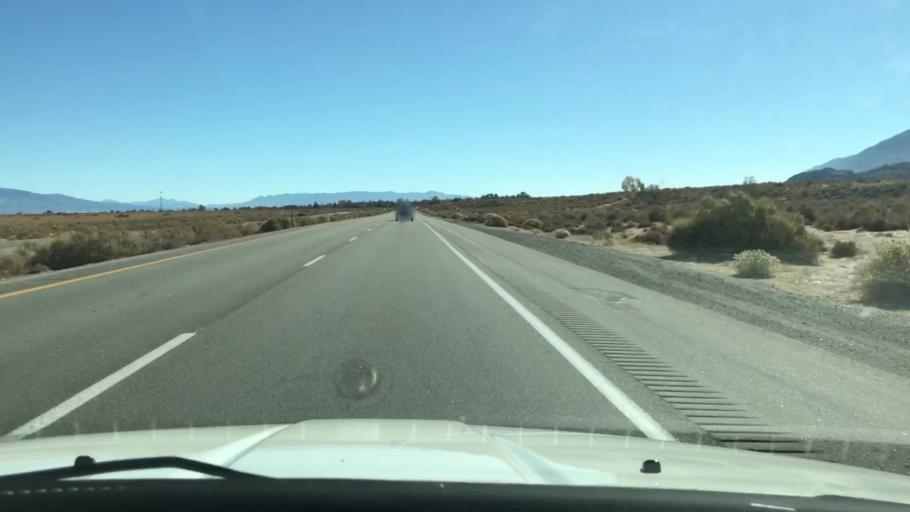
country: US
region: California
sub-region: Inyo County
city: Lone Pine
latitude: 36.6316
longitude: -118.0761
